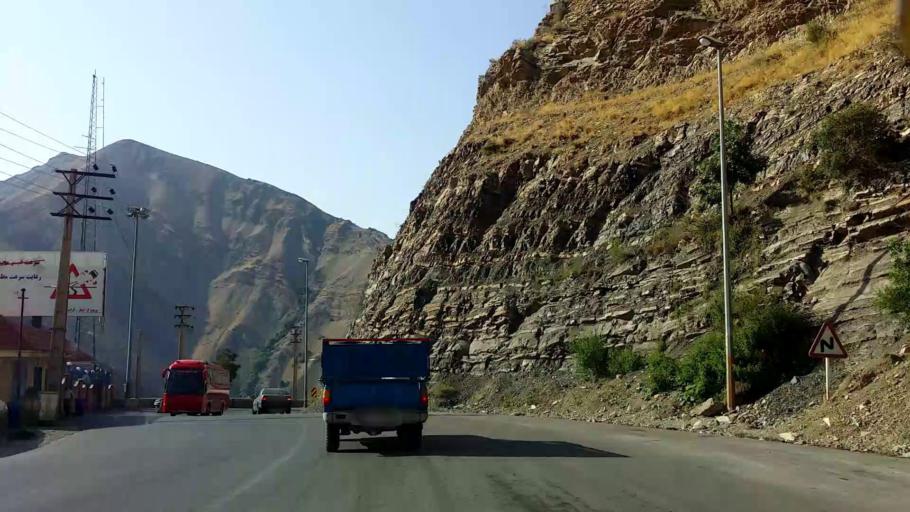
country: IR
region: Alborz
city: Karaj
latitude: 35.9568
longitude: 51.0852
